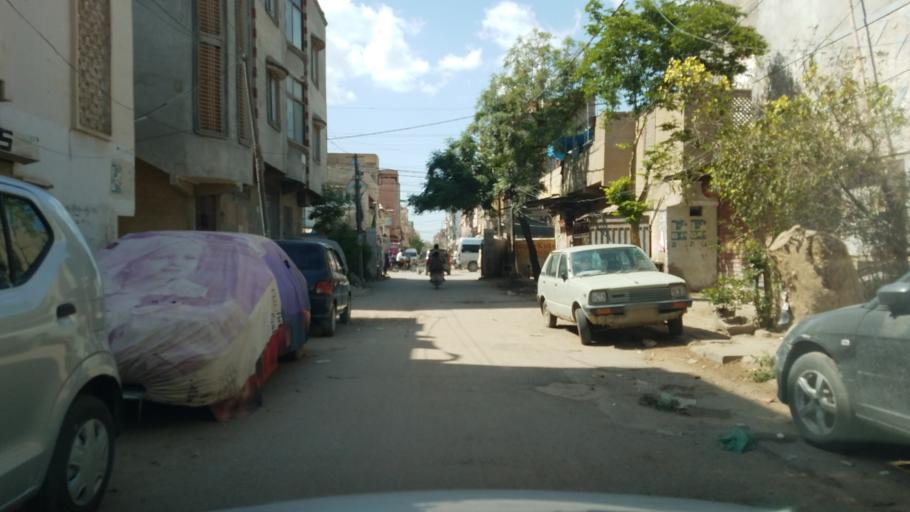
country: PK
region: Sindh
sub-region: Karachi District
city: Karachi
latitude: 24.9478
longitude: 67.0804
